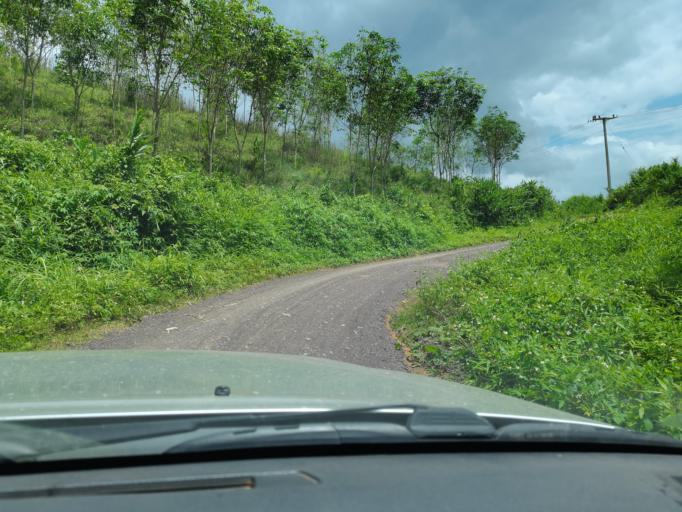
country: LA
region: Loungnamtha
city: Muang Long
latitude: 20.7186
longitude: 101.0142
